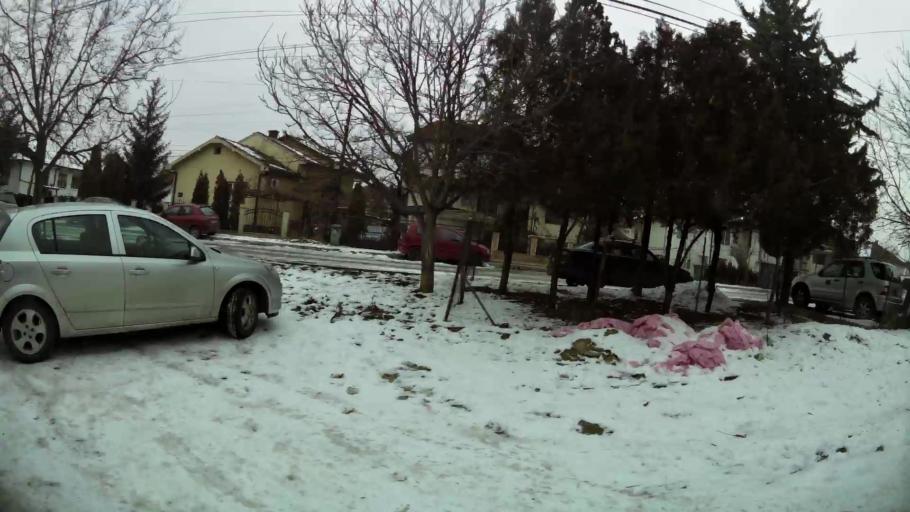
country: MK
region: Butel
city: Butel
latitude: 42.0355
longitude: 21.4493
